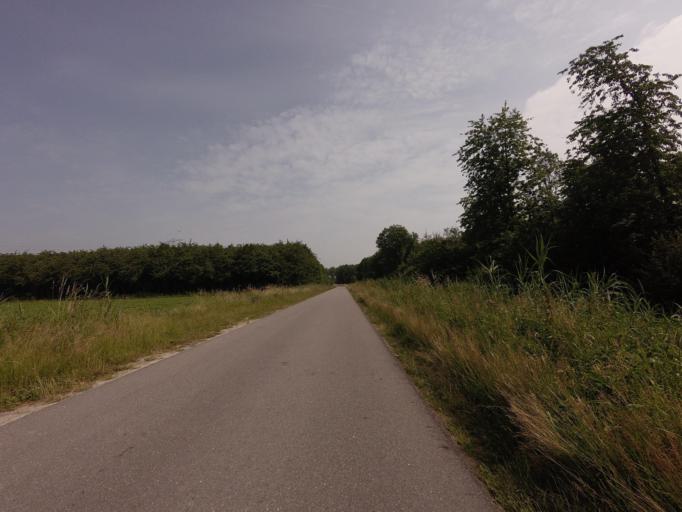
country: NL
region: Flevoland
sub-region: Gemeente Almere
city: Almere Stad
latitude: 52.3827
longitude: 5.2919
